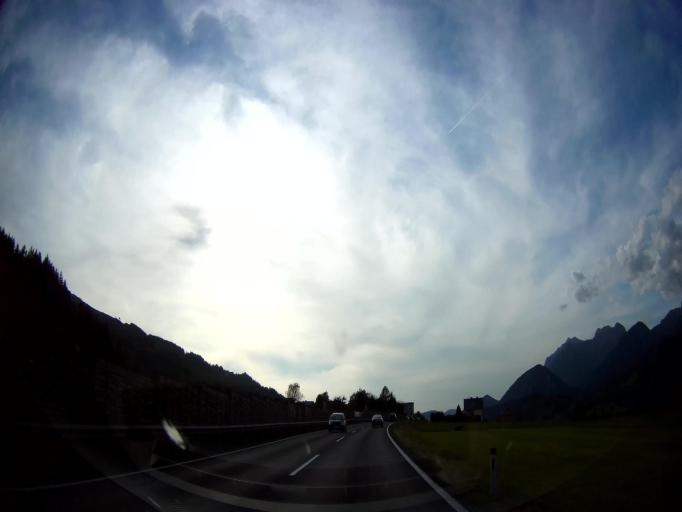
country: AT
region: Styria
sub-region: Politischer Bezirk Liezen
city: Aich
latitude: 47.4135
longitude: 13.8030
